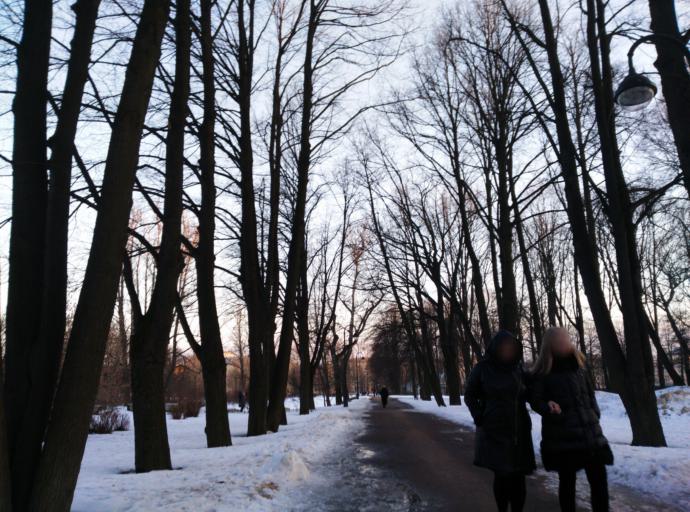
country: RU
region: St.-Petersburg
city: Kupchino
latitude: 59.8685
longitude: 30.3222
